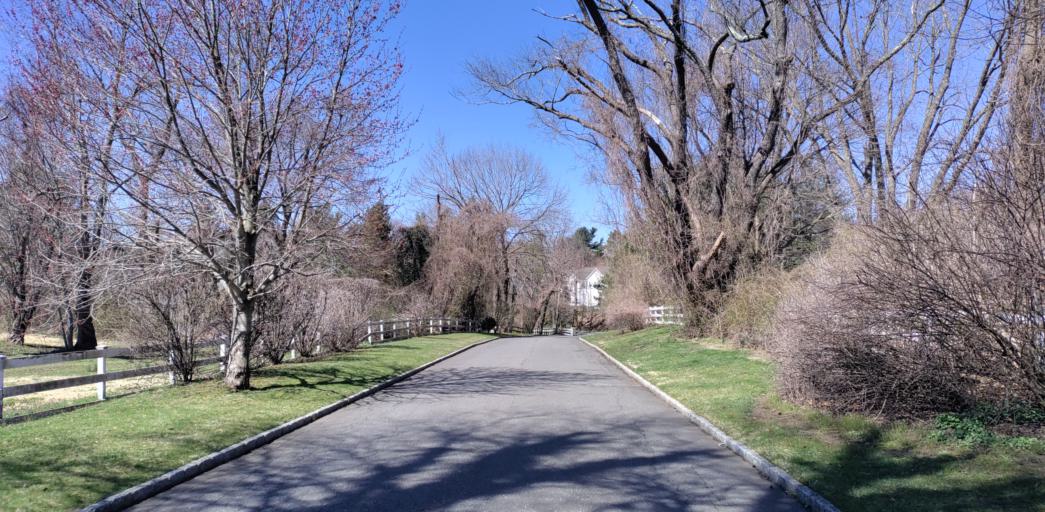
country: US
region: New York
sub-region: Nassau County
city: Old Brookville
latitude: 40.8330
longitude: -73.6018
